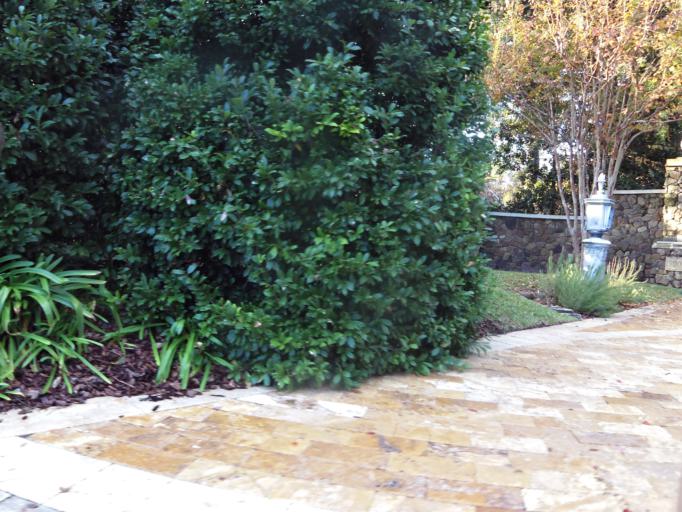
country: US
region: Florida
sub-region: Duval County
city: Jacksonville
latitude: 30.2860
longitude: -81.6601
